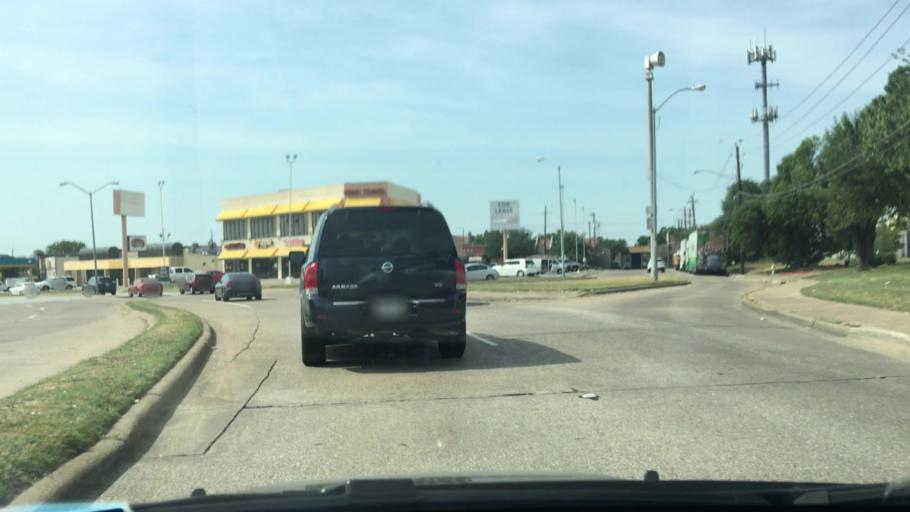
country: US
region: Texas
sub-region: Dallas County
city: Addison
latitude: 32.9309
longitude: -96.8113
